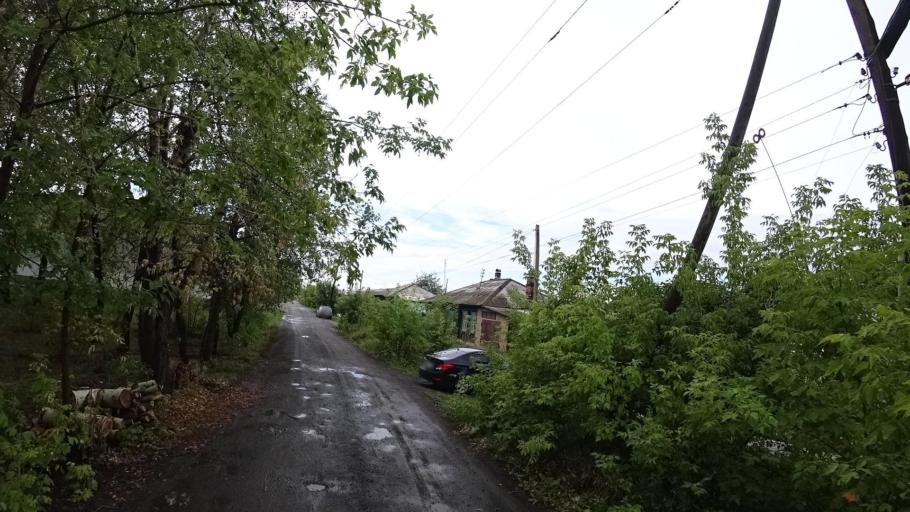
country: RU
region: Sverdlovsk
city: Kamyshlov
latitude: 56.8461
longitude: 62.7243
